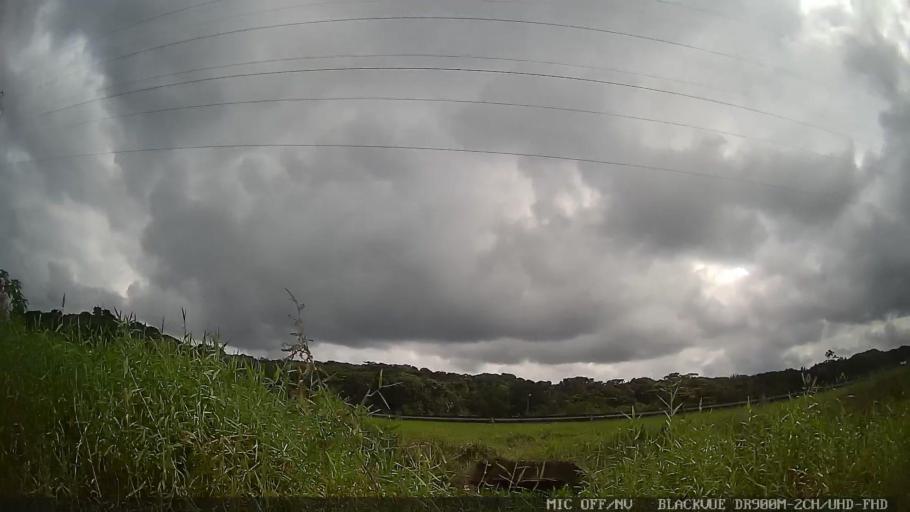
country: BR
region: Sao Paulo
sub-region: Itanhaem
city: Itanhaem
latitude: -24.2029
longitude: -46.8490
